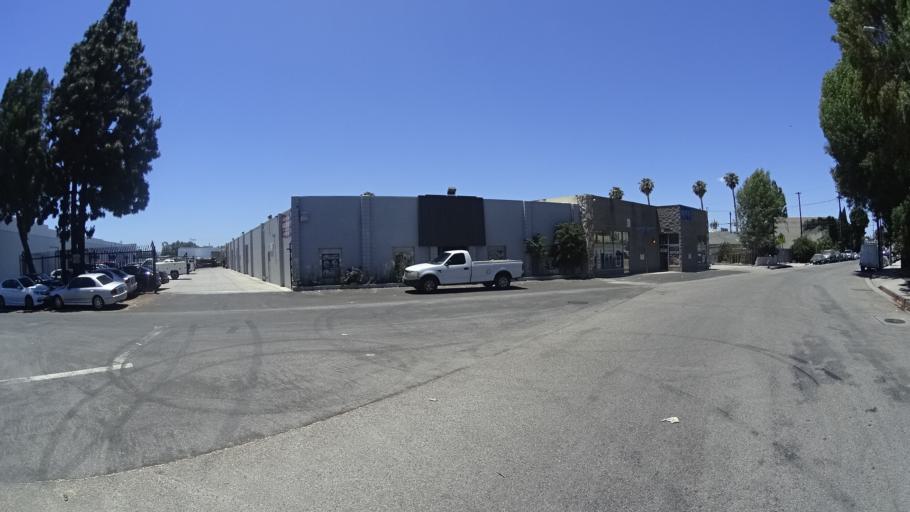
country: US
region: California
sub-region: Los Angeles County
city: Van Nuys
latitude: 34.2170
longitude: -118.4689
